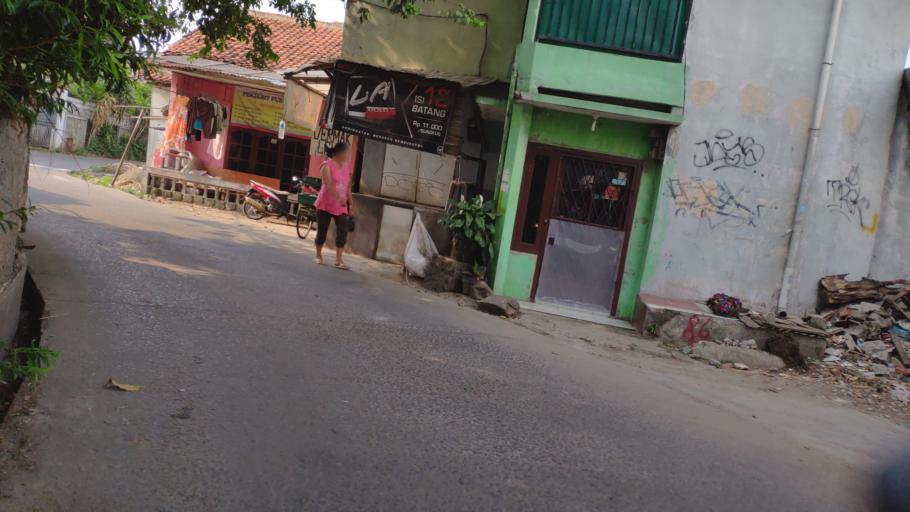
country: ID
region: West Java
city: Pamulang
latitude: -6.3219
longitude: 106.7939
